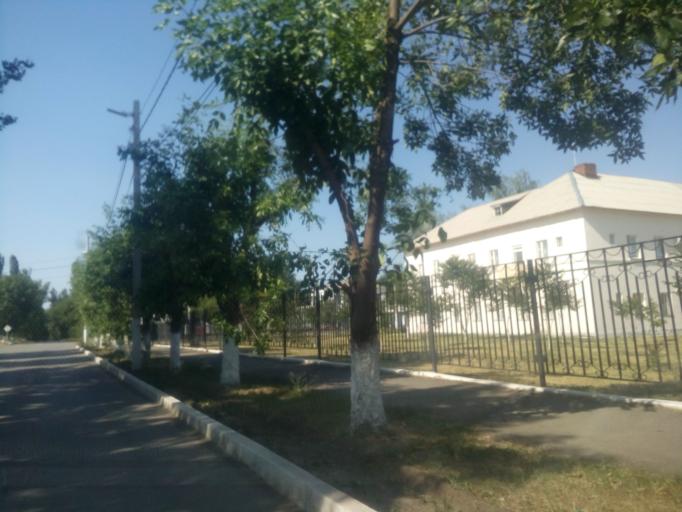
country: RU
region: Rostov
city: Sholokhovskiy
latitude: 48.2820
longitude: 41.0382
